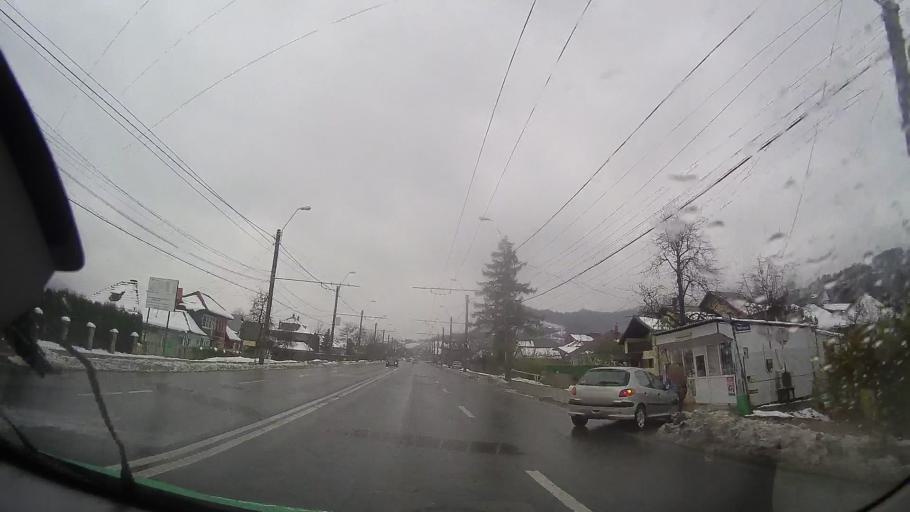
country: RO
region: Neamt
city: Piatra Neamt
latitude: 46.9393
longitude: 26.3355
